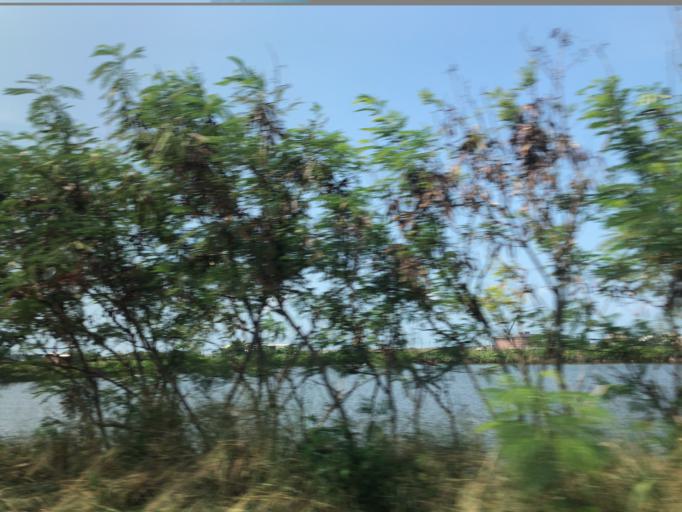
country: TW
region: Taiwan
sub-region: Chiayi
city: Taibao
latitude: 23.4651
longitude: 120.1514
